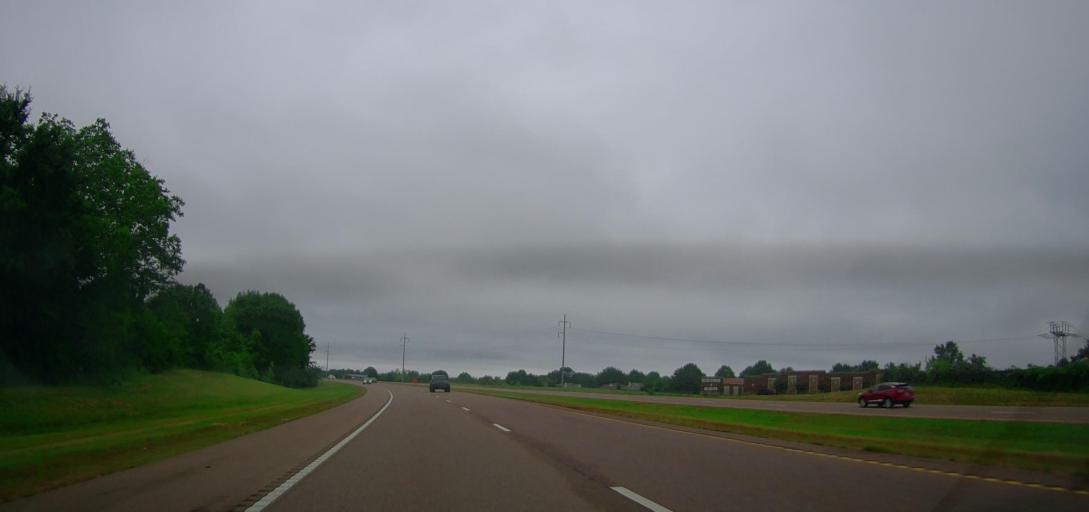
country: US
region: Mississippi
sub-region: De Soto County
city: Olive Branch
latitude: 34.9682
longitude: -89.8057
